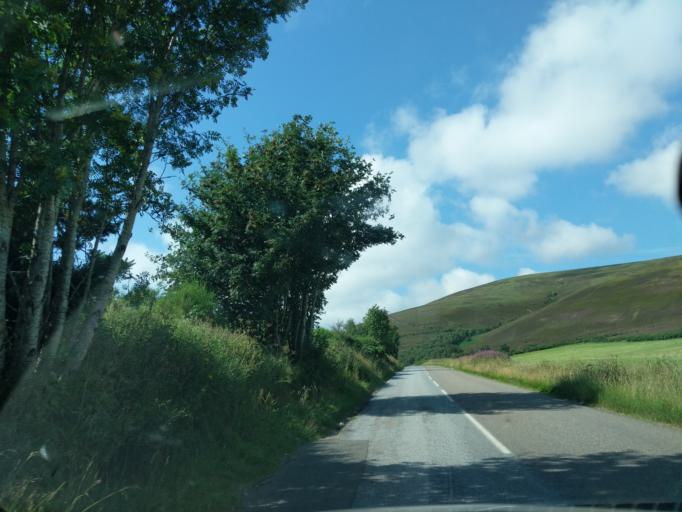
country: GB
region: Scotland
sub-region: Moray
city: Dufftown
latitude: 57.4249
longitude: -3.1567
